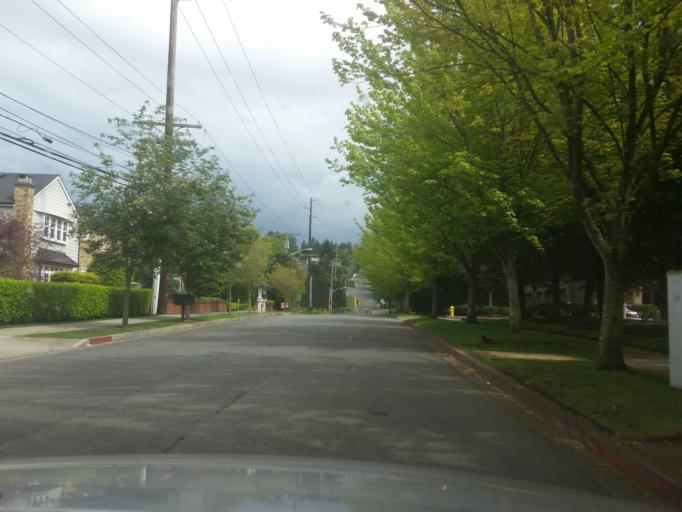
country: US
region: Washington
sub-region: King County
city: Kirkland
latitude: 47.6754
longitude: -122.1941
